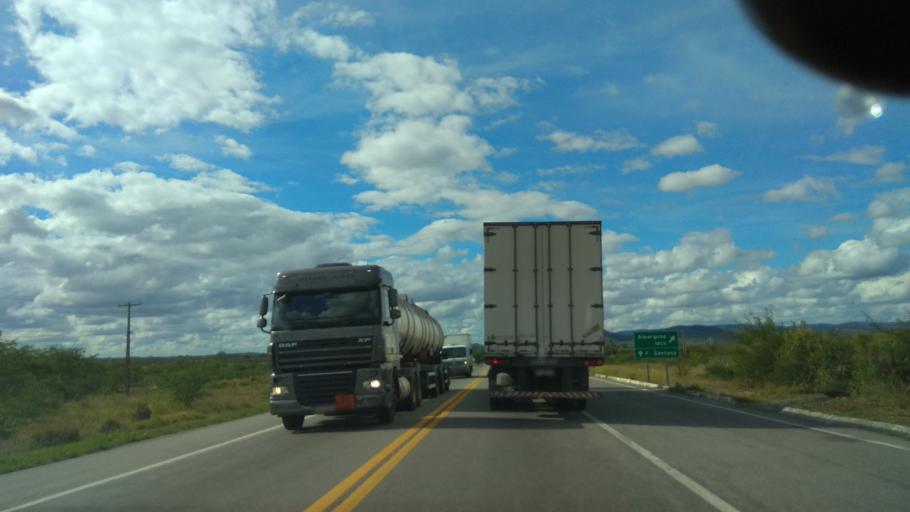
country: BR
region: Bahia
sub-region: Amargosa
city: Amargosa
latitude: -12.8494
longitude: -39.8429
